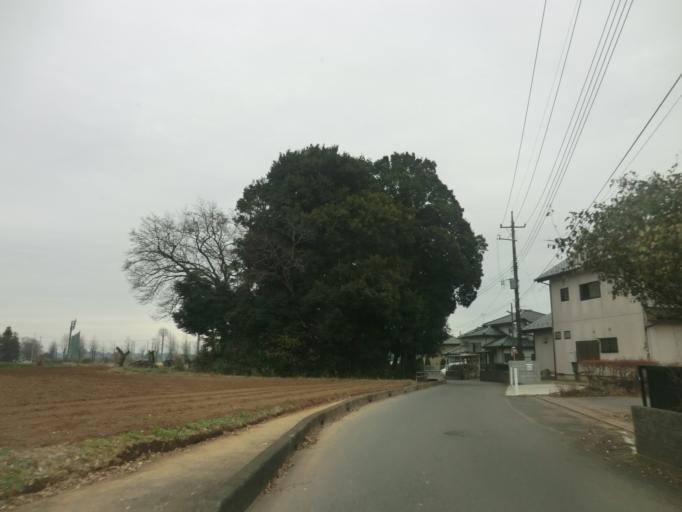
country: JP
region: Ibaraki
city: Ushiku
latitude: 35.9809
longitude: 140.0996
